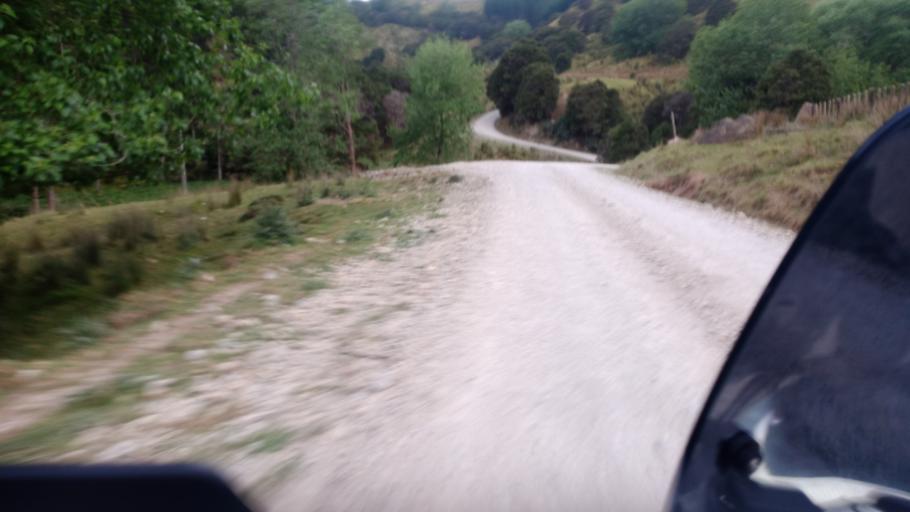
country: NZ
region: Gisborne
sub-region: Gisborne District
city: Gisborne
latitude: -38.4807
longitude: 177.9641
